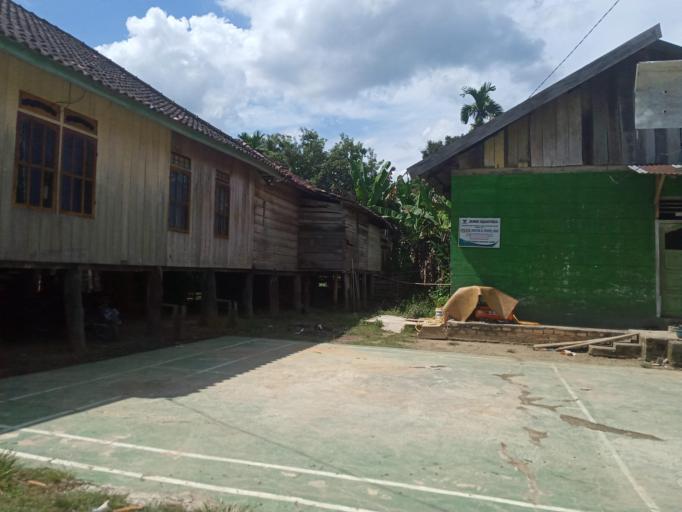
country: ID
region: Jambi
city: Sengeti
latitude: -1.5116
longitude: 103.4341
